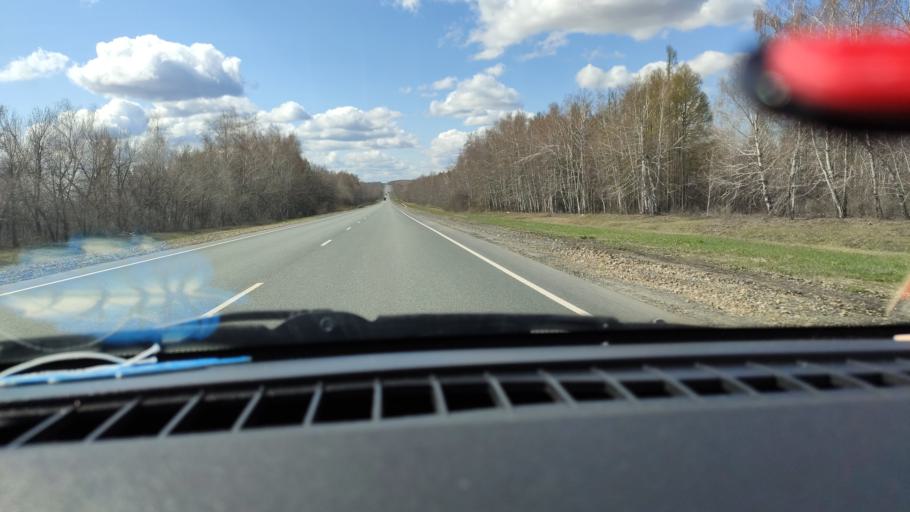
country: RU
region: Saratov
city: Khvalynsk
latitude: 52.5768
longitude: 48.1107
